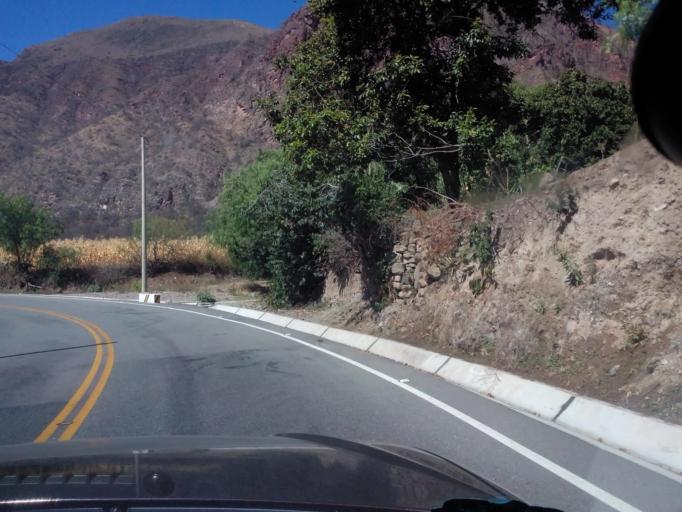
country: PE
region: Ayacucho
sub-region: Provincia de Huamanga
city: Ocros
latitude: -13.4241
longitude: -73.8650
